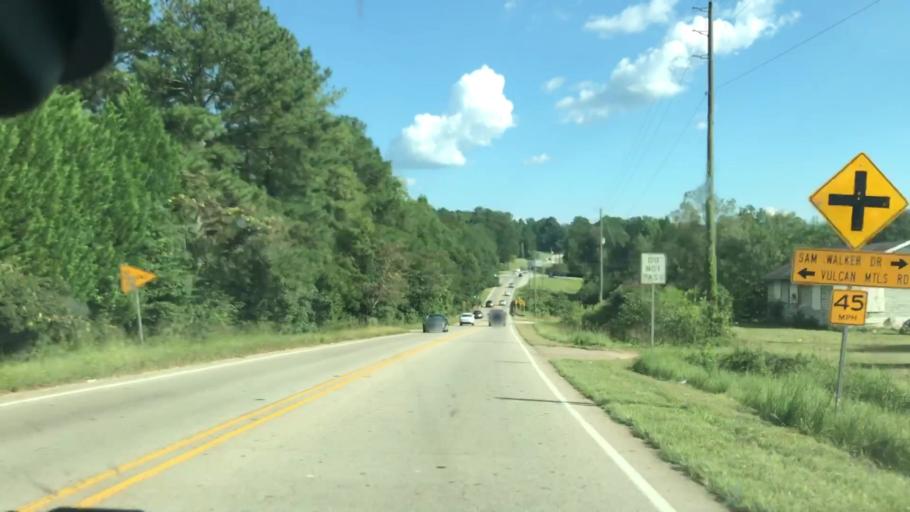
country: US
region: Georgia
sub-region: Troup County
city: La Grange
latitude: 32.9928
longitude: -85.0059
